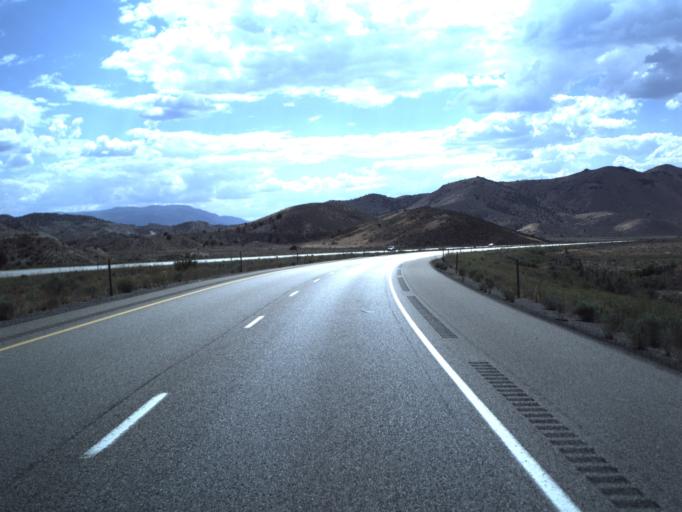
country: US
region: Utah
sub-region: Sevier County
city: Aurora
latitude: 38.8921
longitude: -111.9068
